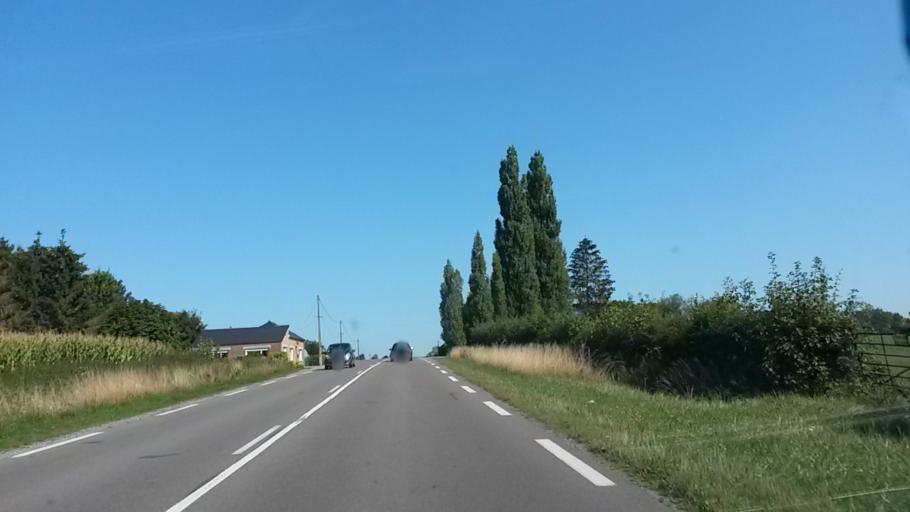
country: FR
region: Nord-Pas-de-Calais
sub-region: Departement du Nord
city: Avesnes-sur-Helpe
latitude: 50.0836
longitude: 3.9298
